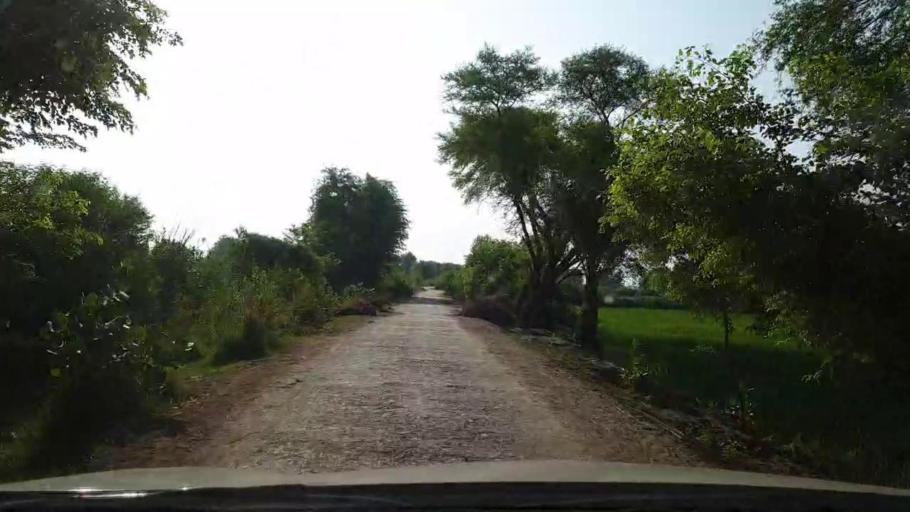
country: PK
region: Sindh
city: Larkana
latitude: 27.5511
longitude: 68.2641
